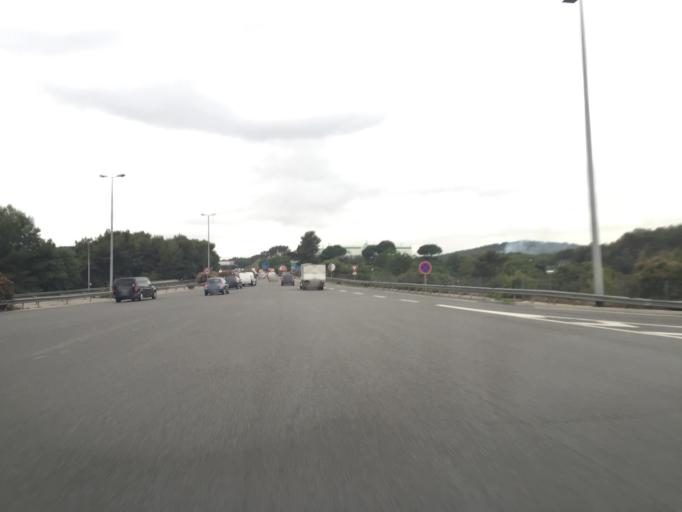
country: FR
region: Provence-Alpes-Cote d'Azur
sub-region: Departement des Alpes-Maritimes
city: Vallauris
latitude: 43.6043
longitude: 7.0644
